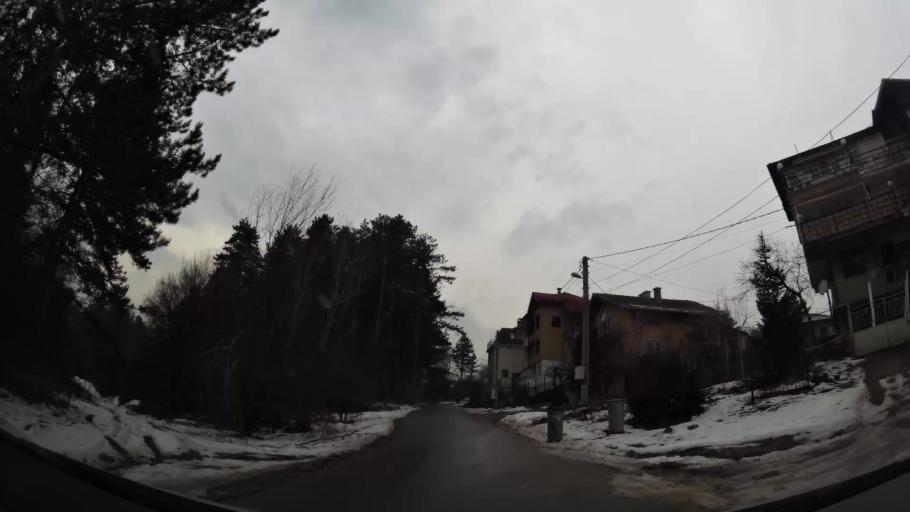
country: BG
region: Sofiya
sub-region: Obshtina Bozhurishte
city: Bozhurishte
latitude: 42.6696
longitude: 23.2382
